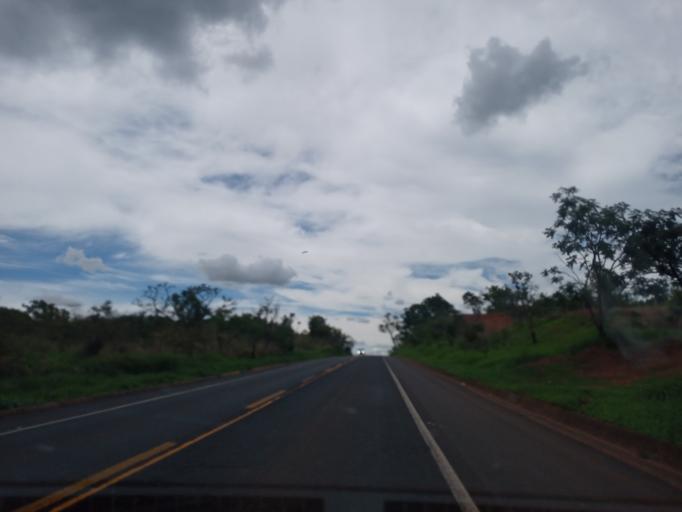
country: BR
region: Minas Gerais
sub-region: Uberlandia
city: Uberlandia
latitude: -19.1741
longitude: -47.8905
